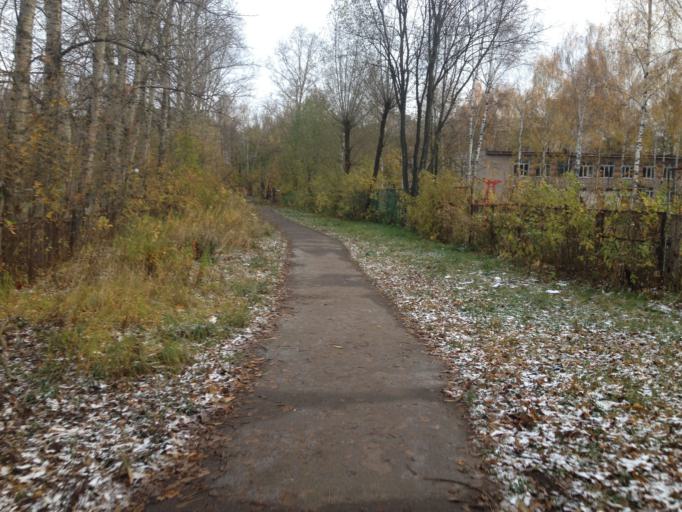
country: RU
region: Ivanovo
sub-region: Gorod Ivanovo
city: Ivanovo
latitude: 56.9598
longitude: 40.9976
